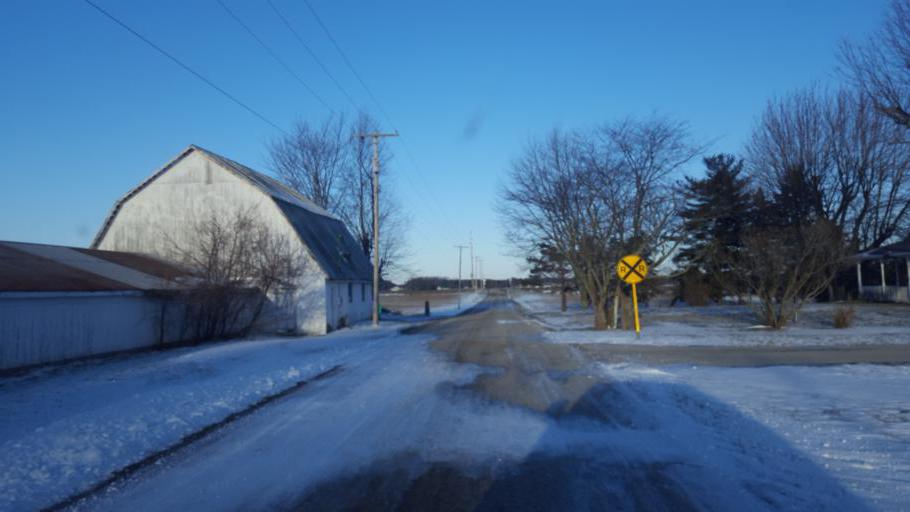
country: US
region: Ohio
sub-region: Morrow County
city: Cardington
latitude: 40.5164
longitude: -82.8842
